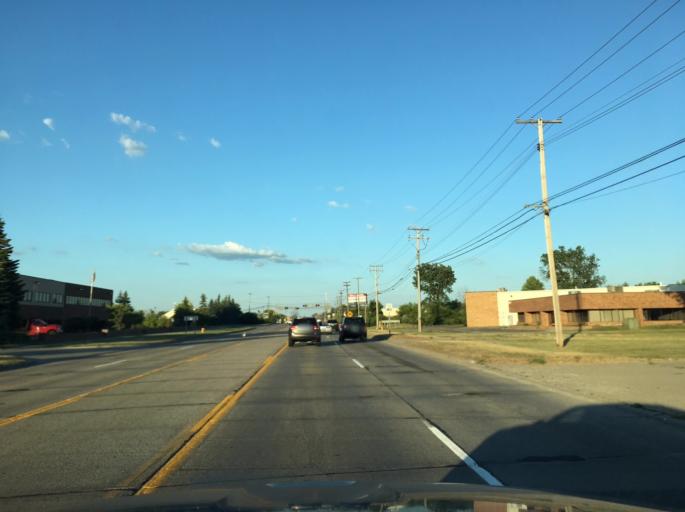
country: US
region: Michigan
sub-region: Macomb County
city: Fraser
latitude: 42.5540
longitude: -82.9293
